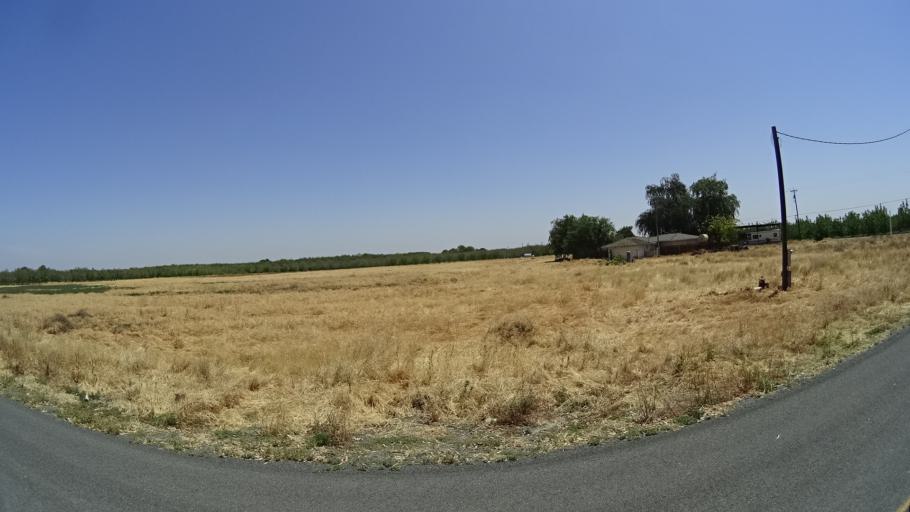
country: US
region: California
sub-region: Kings County
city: Armona
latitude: 36.2554
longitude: -119.7268
